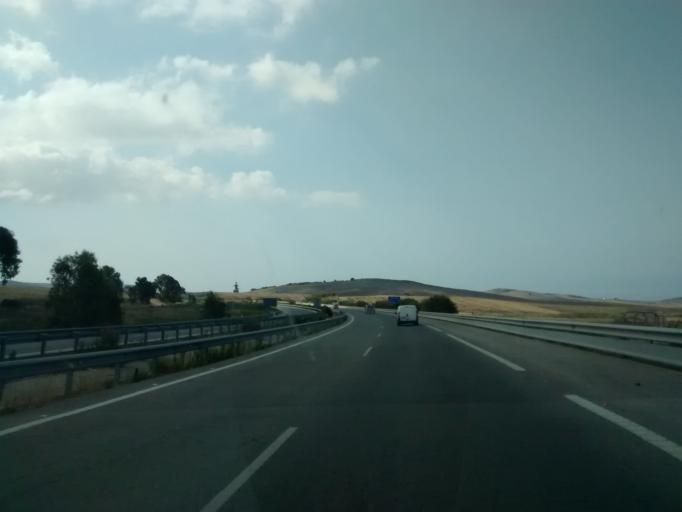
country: ES
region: Andalusia
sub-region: Provincia de Cadiz
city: Conil de la Frontera
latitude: 36.2651
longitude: -6.0296
